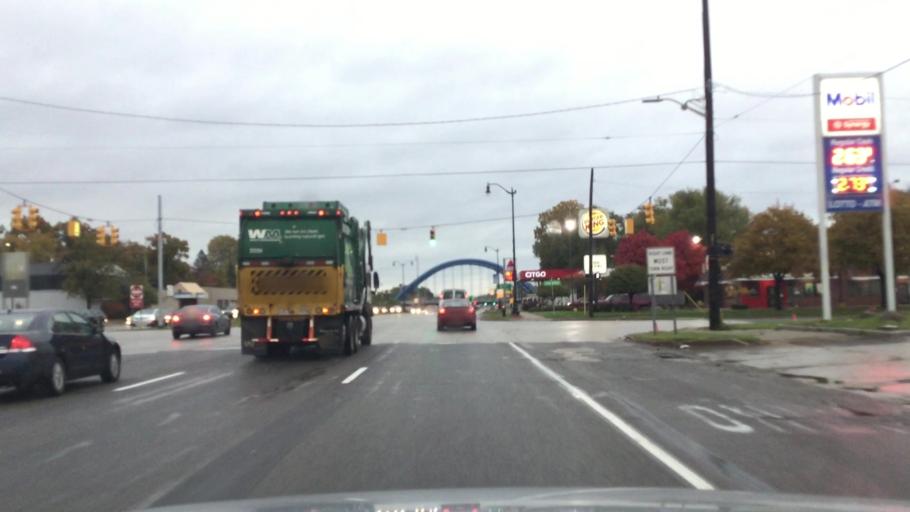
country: US
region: Michigan
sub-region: Wayne County
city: Taylor
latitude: 42.2694
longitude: -83.2706
